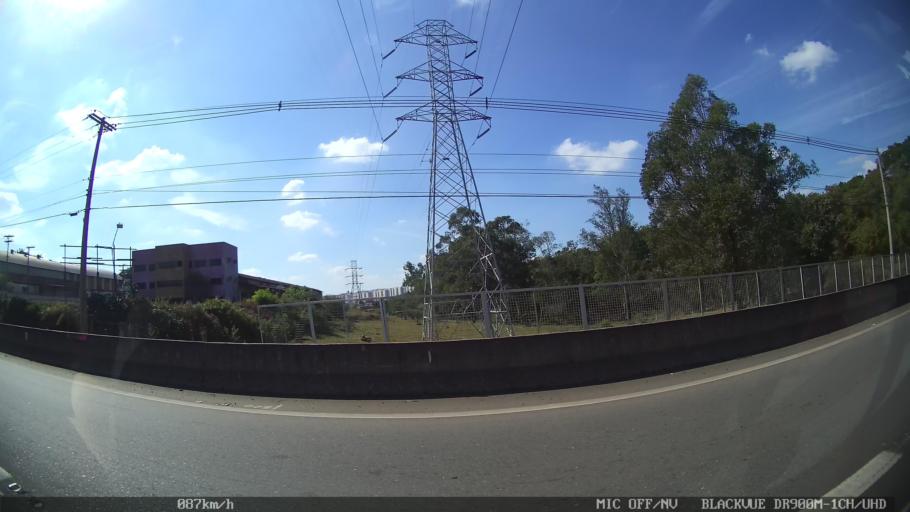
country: BR
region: Sao Paulo
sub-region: Hortolandia
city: Hortolandia
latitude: -22.8350
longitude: -47.1742
